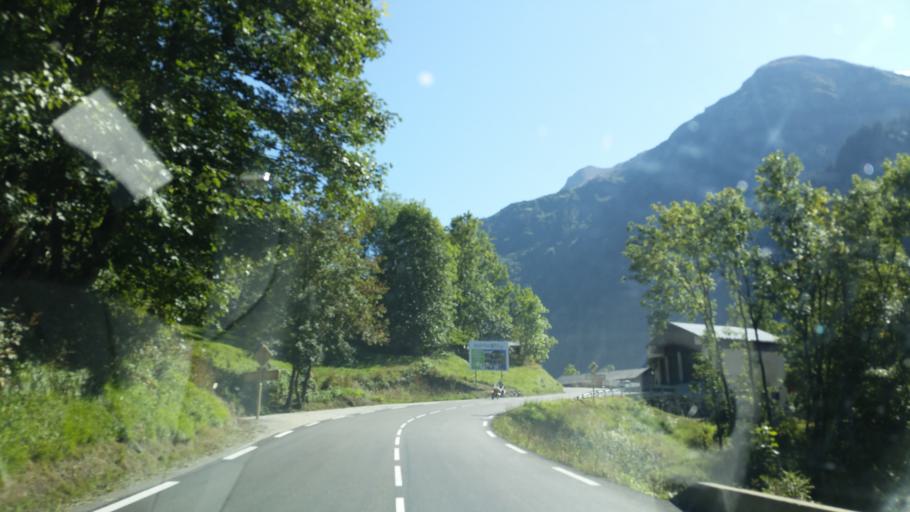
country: FR
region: Rhone-Alpes
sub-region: Departement de la Savoie
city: Tignes
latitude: 45.5758
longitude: 6.8844
